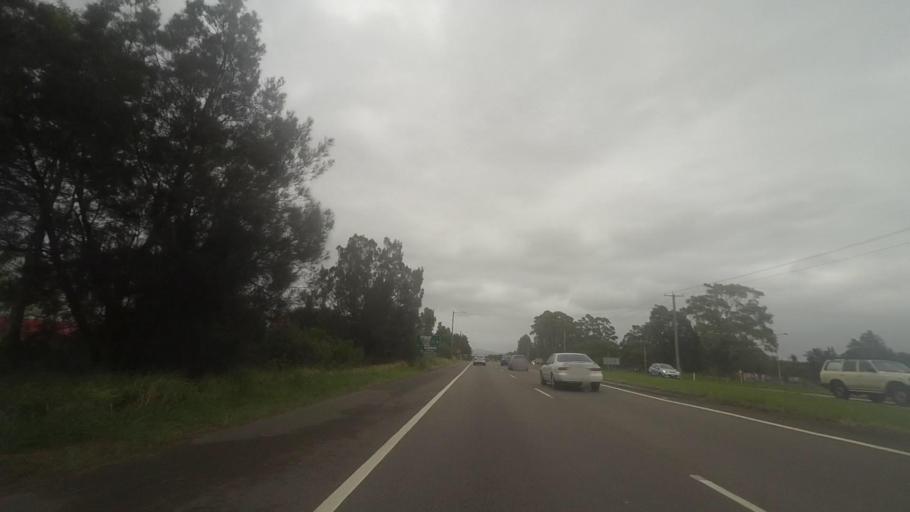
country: AU
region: New South Wales
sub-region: Newcastle
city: Beresfield
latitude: -32.8145
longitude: 151.7007
